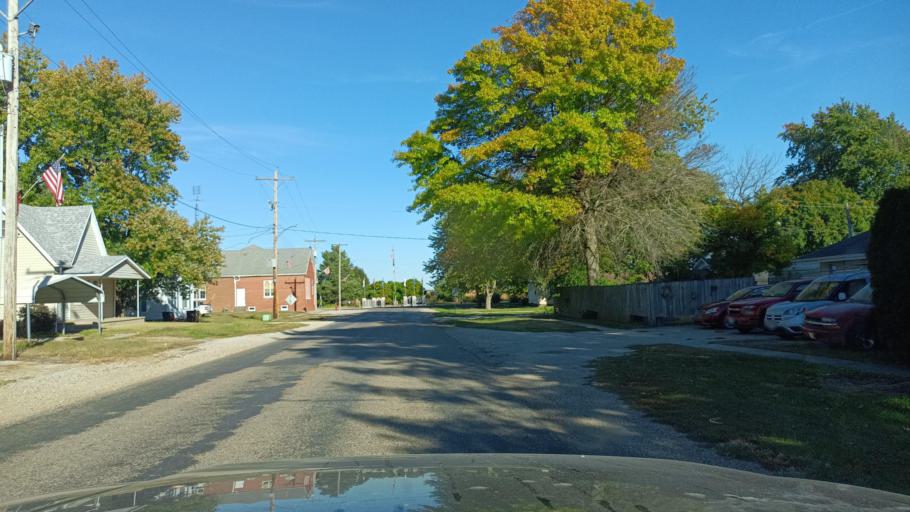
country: US
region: Illinois
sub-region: De Witt County
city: Clinton
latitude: 40.2208
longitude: -88.9604
